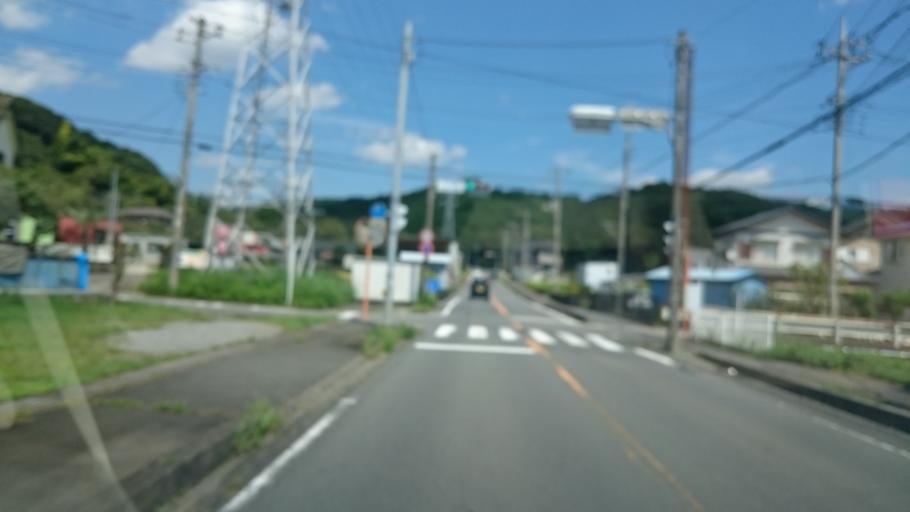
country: JP
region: Shizuoka
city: Mishima
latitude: 35.1971
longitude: 138.9241
